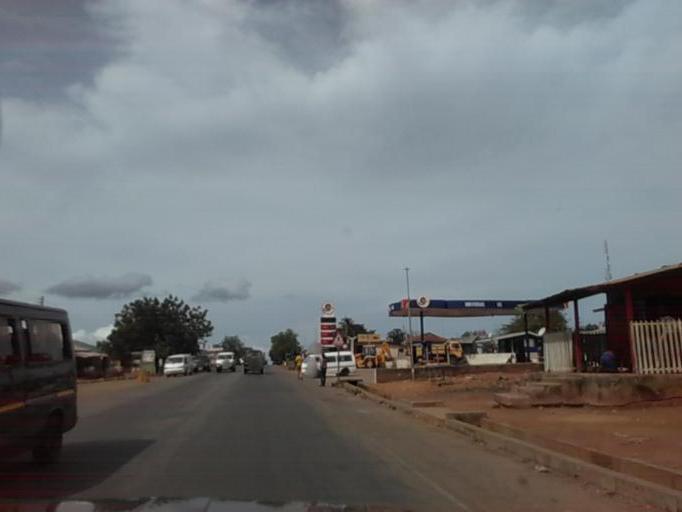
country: GH
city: Akropong
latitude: 6.2052
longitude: 0.0796
